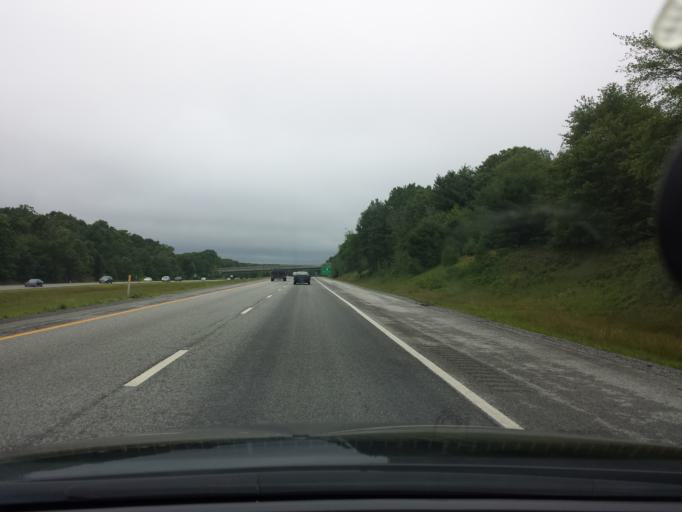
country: US
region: Rhode Island
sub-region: Kent County
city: West Greenwich
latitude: 41.5880
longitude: -71.6594
